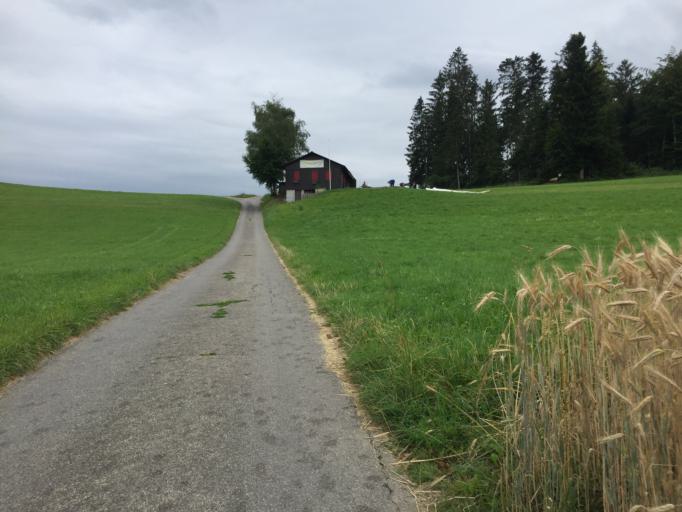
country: CH
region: Bern
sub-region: Bern-Mittelland District
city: Biglen
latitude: 46.9057
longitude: 7.6223
